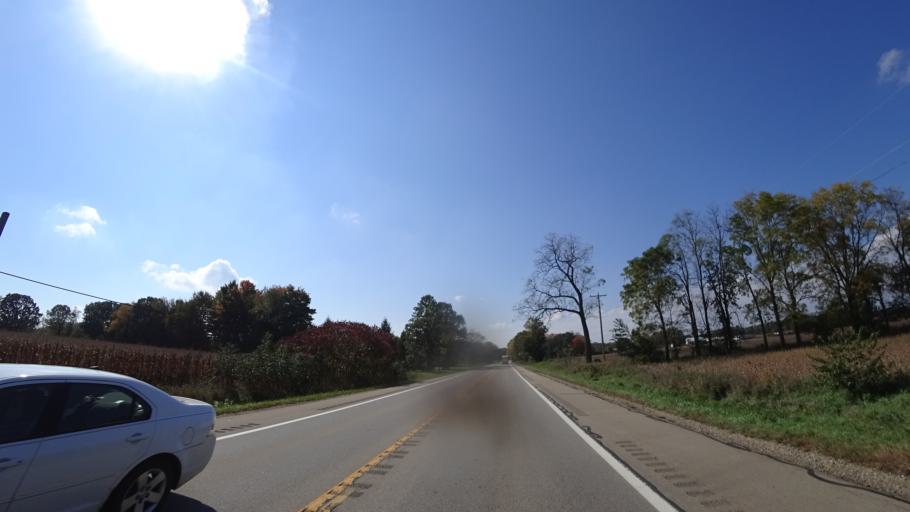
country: US
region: Michigan
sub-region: Jackson County
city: Spring Arbor
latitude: 42.2000
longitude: -84.5738
